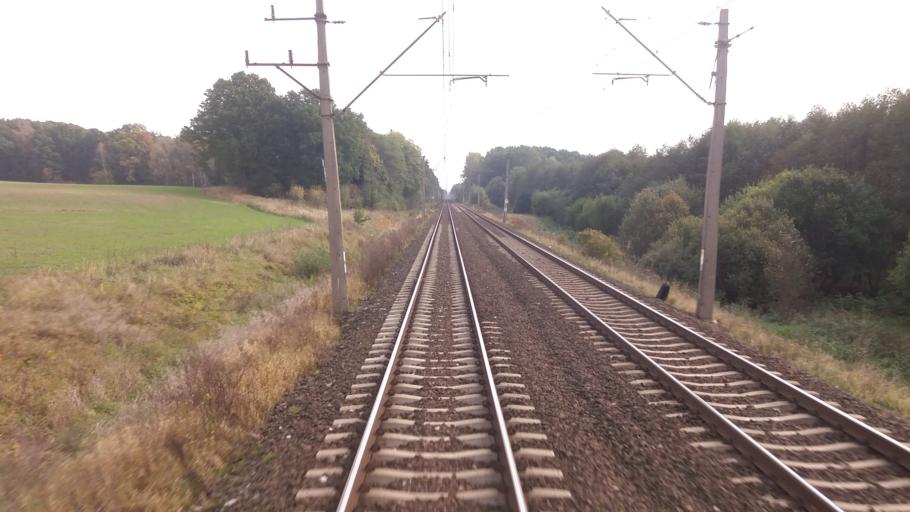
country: PL
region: West Pomeranian Voivodeship
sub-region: Powiat stargardzki
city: Dolice
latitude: 53.1901
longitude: 15.2429
